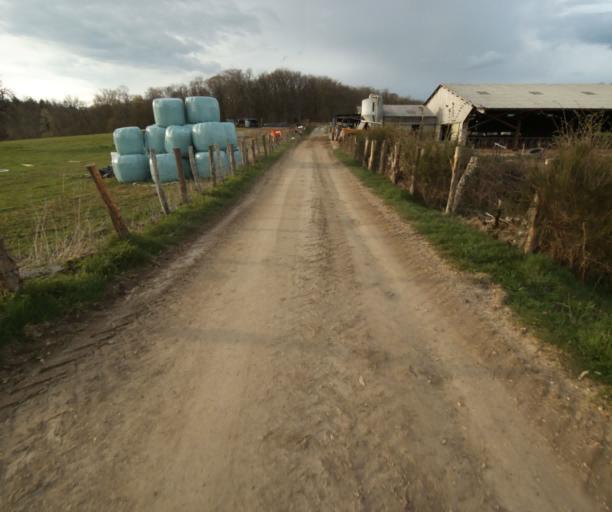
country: FR
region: Limousin
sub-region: Departement de la Correze
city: Argentat
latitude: 45.2290
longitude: 1.9502
